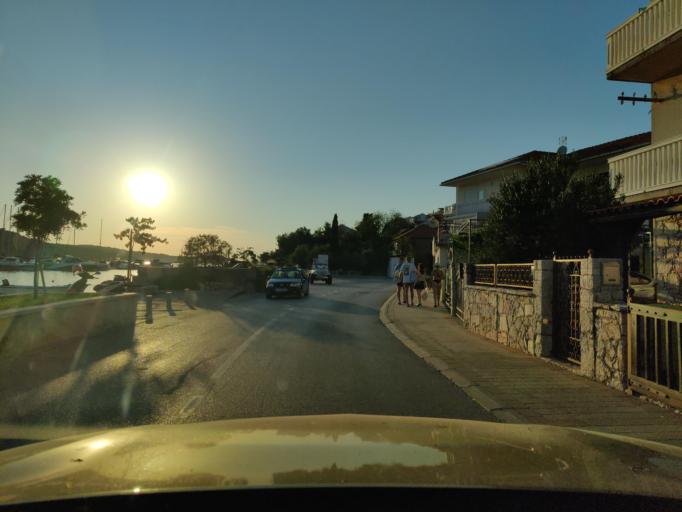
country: HR
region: Sibensko-Kniniska
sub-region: Grad Sibenik
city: Tisno
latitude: 43.8001
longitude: 15.6405
